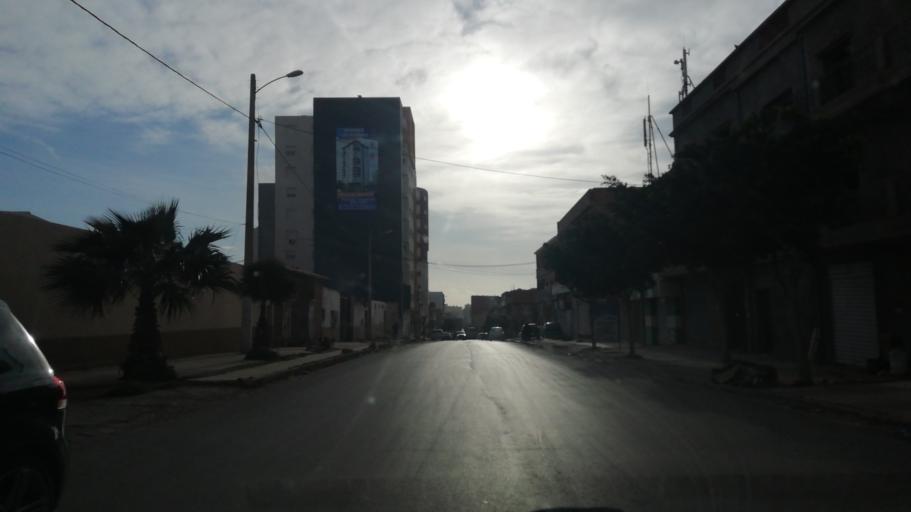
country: DZ
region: Oran
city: Bir el Djir
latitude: 35.7318
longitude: -0.5769
